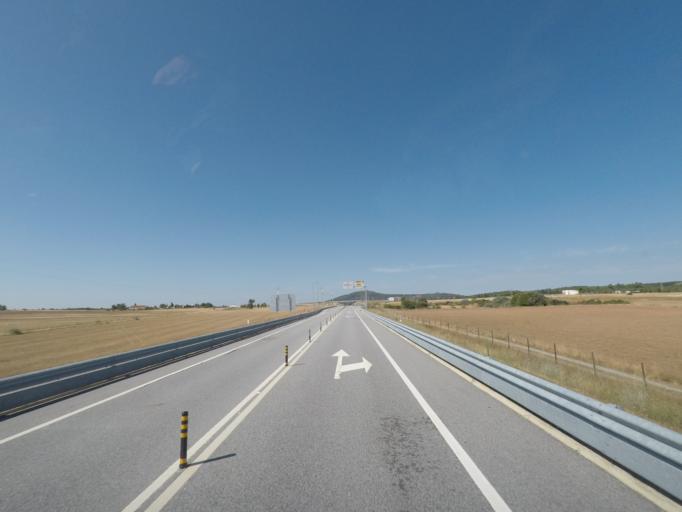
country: ES
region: Castille and Leon
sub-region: Provincia de Salamanca
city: Villarino de los Aires
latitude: 41.3577
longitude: -6.5668
